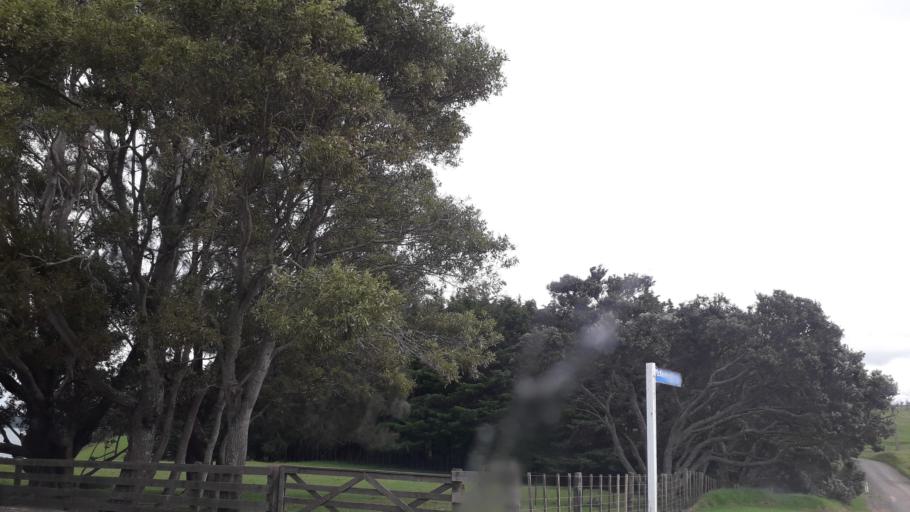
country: NZ
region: Northland
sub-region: Far North District
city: Kerikeri
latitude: -35.1519
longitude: 174.0404
